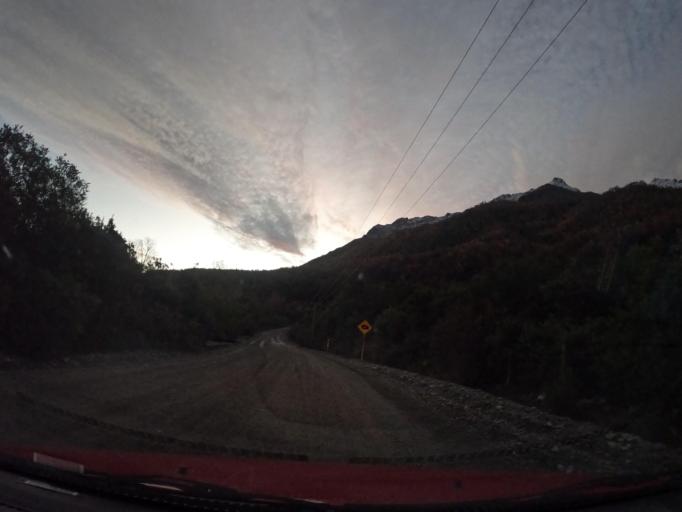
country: CL
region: Maule
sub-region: Provincia de Linares
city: Colbun
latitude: -35.8567
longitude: -71.2024
